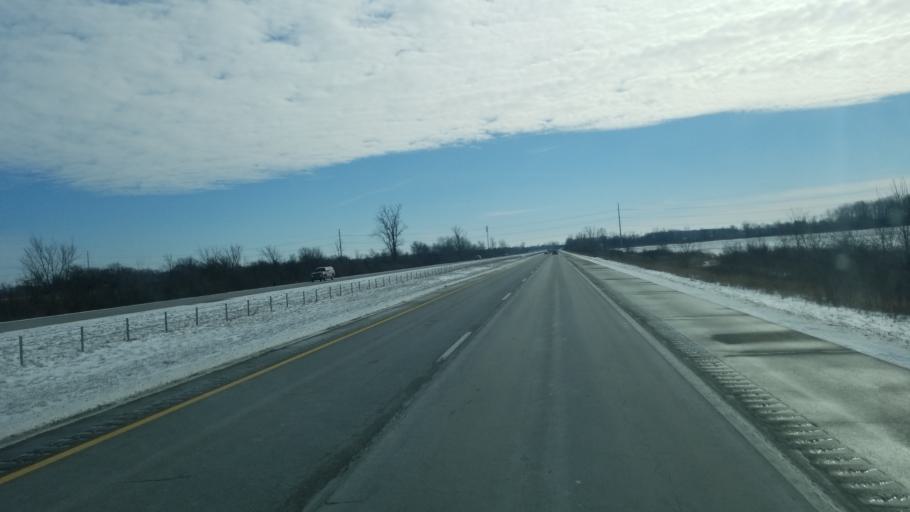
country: US
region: Michigan
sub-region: Washtenaw County
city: Milan
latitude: 42.1263
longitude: -83.6831
